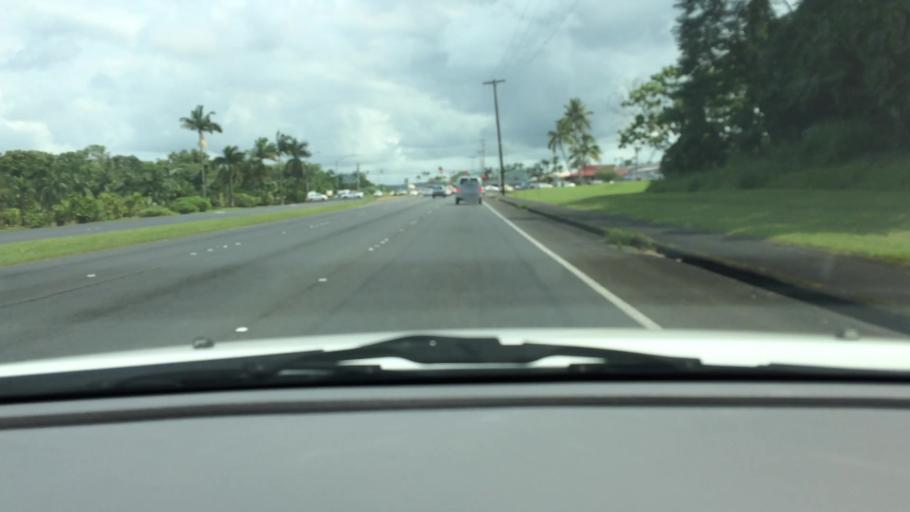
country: US
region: Hawaii
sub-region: Hawaii County
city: Hilo
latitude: 19.6971
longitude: -155.0655
